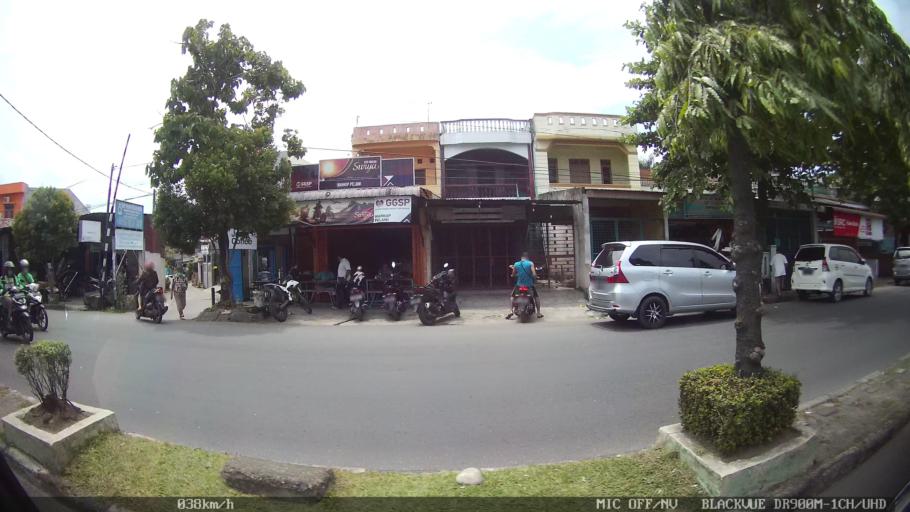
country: ID
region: North Sumatra
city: Medan
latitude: 3.5432
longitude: 98.6565
